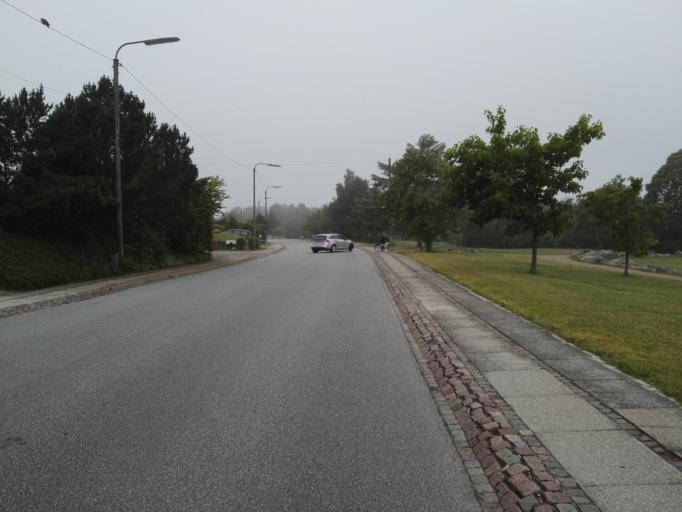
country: DK
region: Capital Region
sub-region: Ballerup Kommune
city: Ballerup
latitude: 55.7394
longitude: 12.3765
